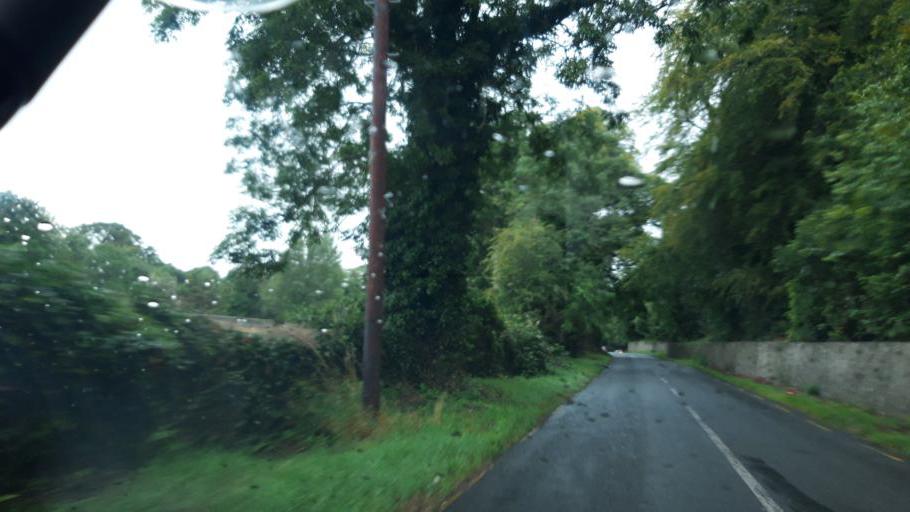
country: IE
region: Leinster
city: Hartstown
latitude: 53.3674
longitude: -6.4234
